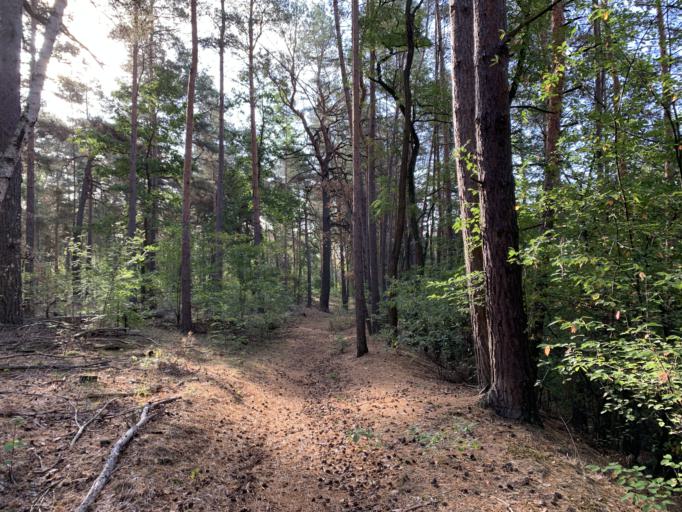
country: DE
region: Berlin
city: Wannsee
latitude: 52.4035
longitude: 13.1786
